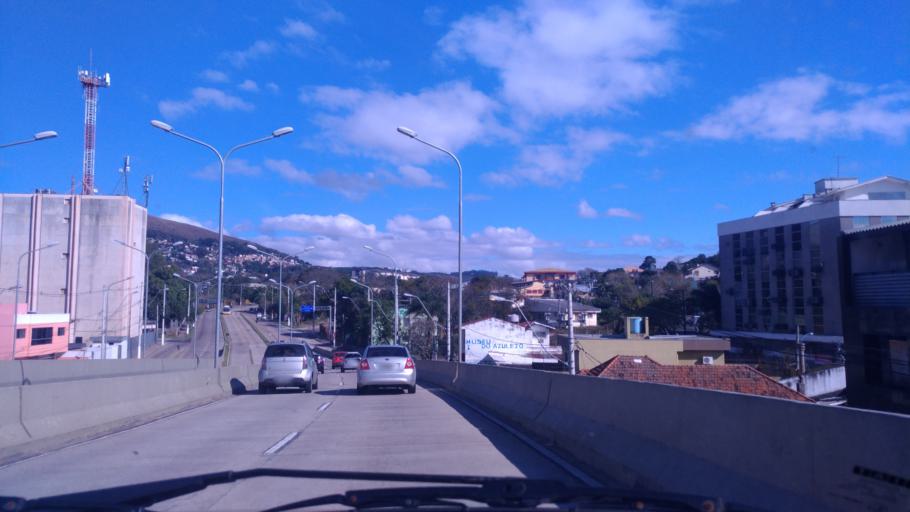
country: BR
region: Rio Grande do Sul
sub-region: Porto Alegre
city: Porto Alegre
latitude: -30.0642
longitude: -51.1862
